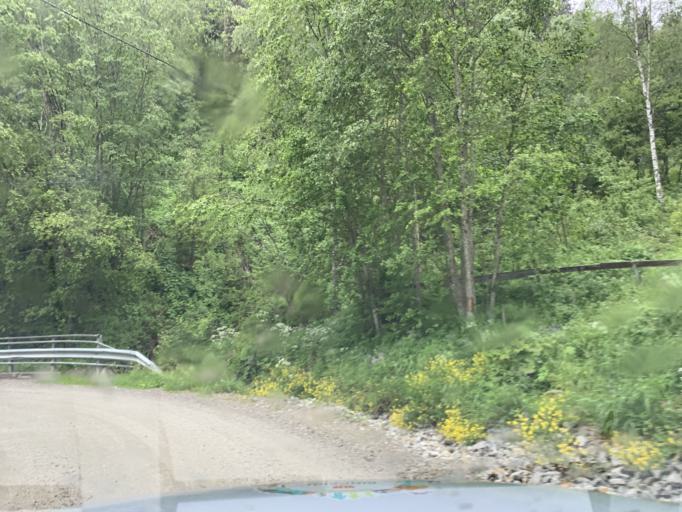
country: NO
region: Oppland
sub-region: Oyer
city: Tretten
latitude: 61.3935
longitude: 10.2743
